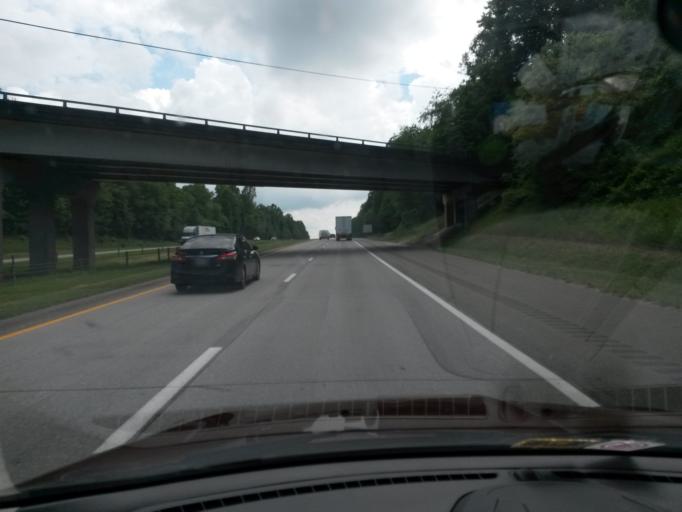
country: US
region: North Carolina
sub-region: Surry County
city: Elkin
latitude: 36.3015
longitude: -80.8093
